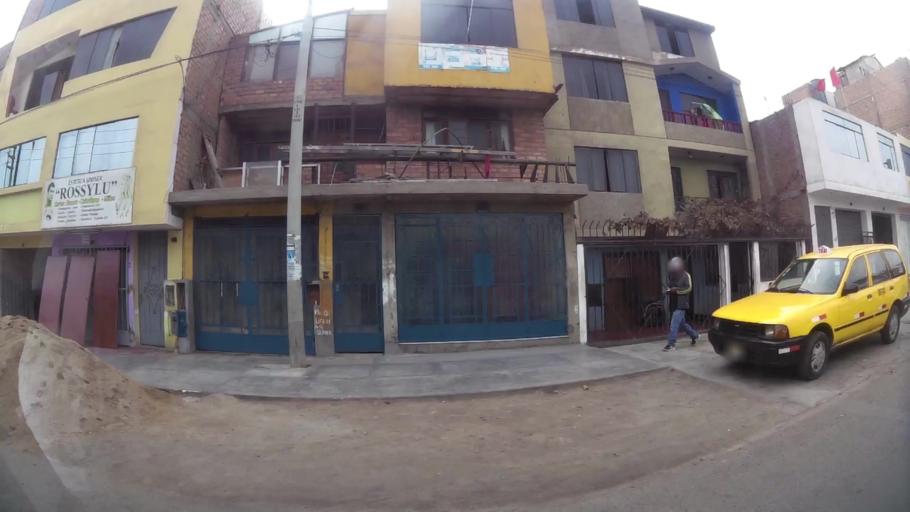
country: PE
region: Lima
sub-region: Lima
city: Independencia
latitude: -12.0139
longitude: -77.0886
